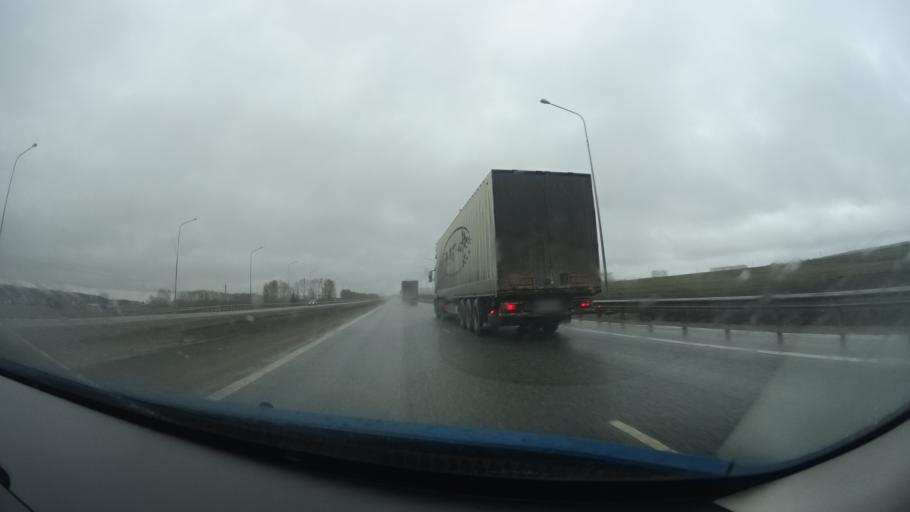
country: RU
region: Bashkortostan
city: Buzdyak
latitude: 54.7155
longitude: 54.8896
